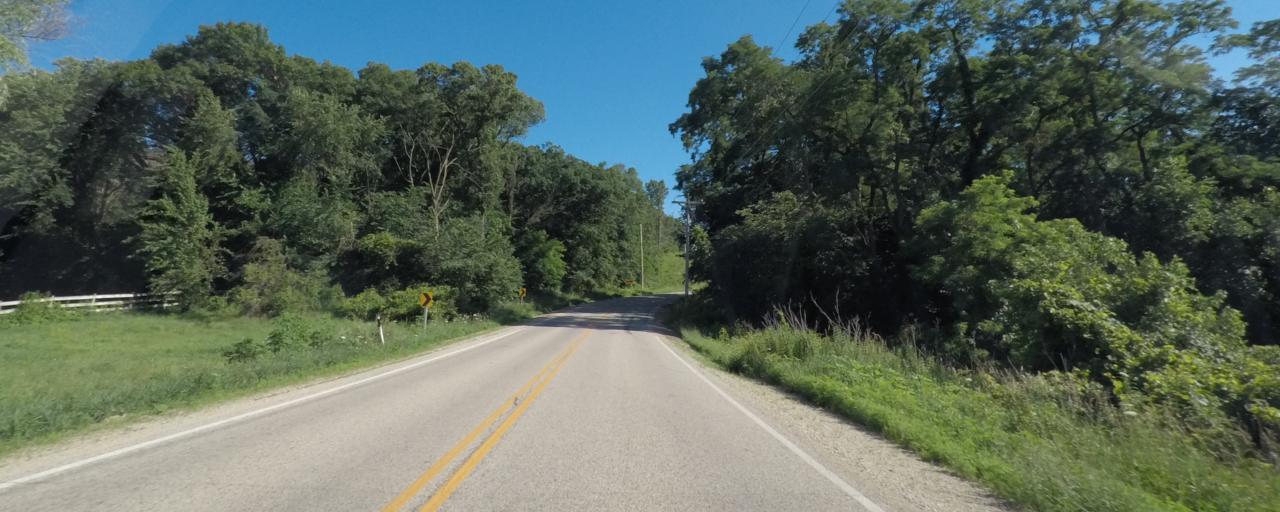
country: US
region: Wisconsin
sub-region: Rock County
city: Edgerton
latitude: 42.7454
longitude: -89.1305
